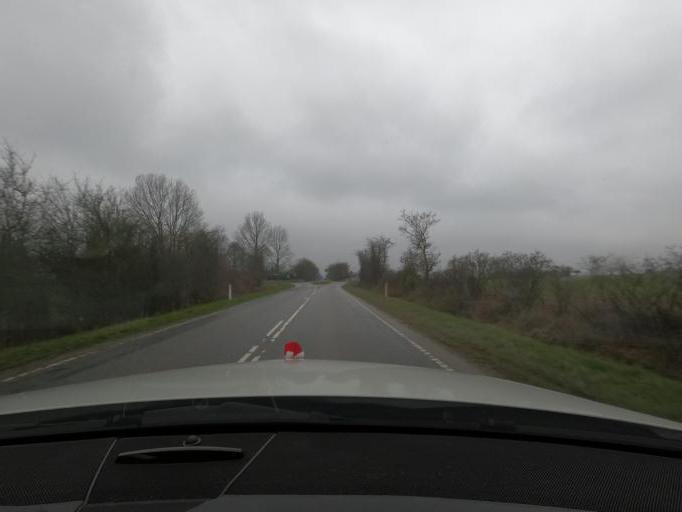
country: DK
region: South Denmark
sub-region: Haderslev Kommune
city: Starup
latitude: 55.2178
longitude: 9.6072
